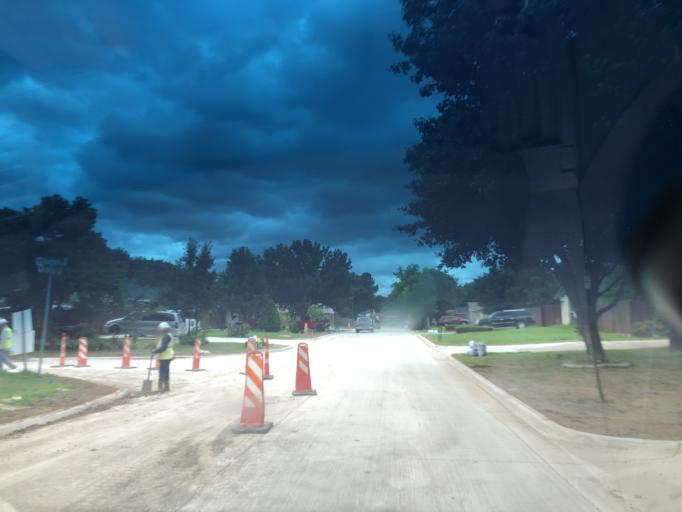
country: US
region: Texas
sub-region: Dallas County
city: Grand Prairie
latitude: 32.6947
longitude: -97.0128
